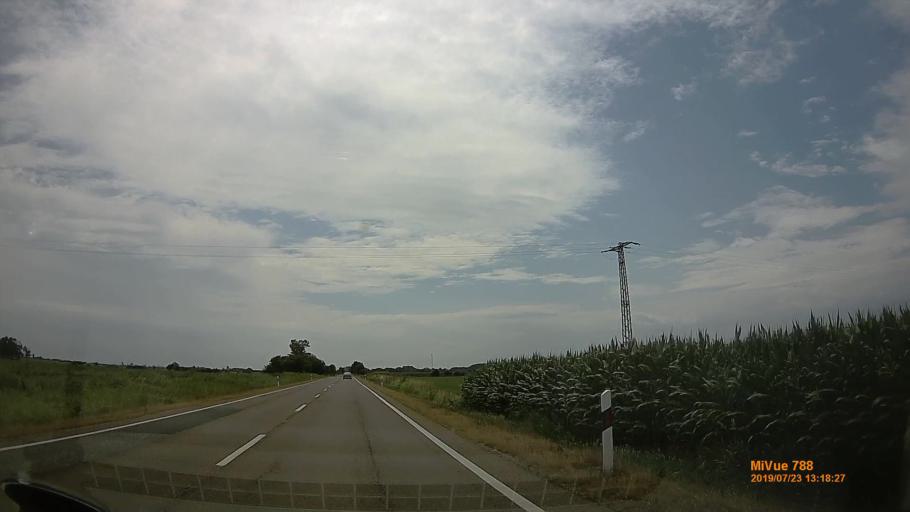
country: HU
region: Hajdu-Bihar
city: Polgar
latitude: 47.8854
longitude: 21.1492
